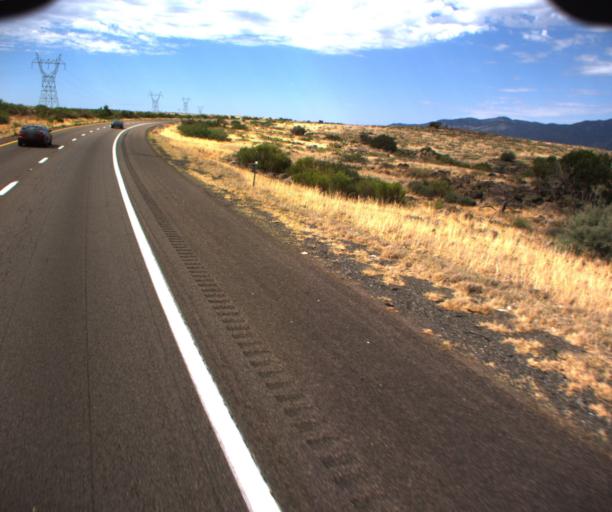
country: US
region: Arizona
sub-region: Yavapai County
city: Cordes Lakes
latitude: 34.2177
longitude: -112.1116
